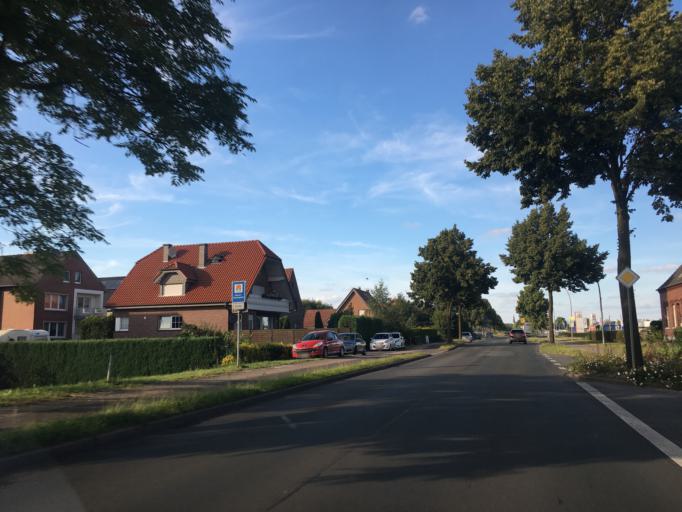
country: DE
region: North Rhine-Westphalia
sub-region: Regierungsbezirk Munster
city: Dulmen
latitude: 51.8115
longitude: 7.2506
